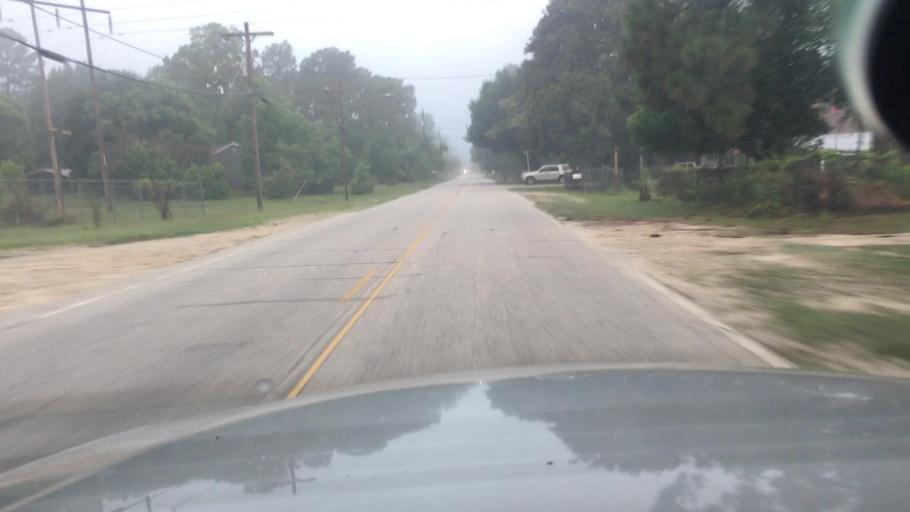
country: US
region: North Carolina
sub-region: Cumberland County
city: Fayetteville
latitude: 35.0157
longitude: -78.9134
